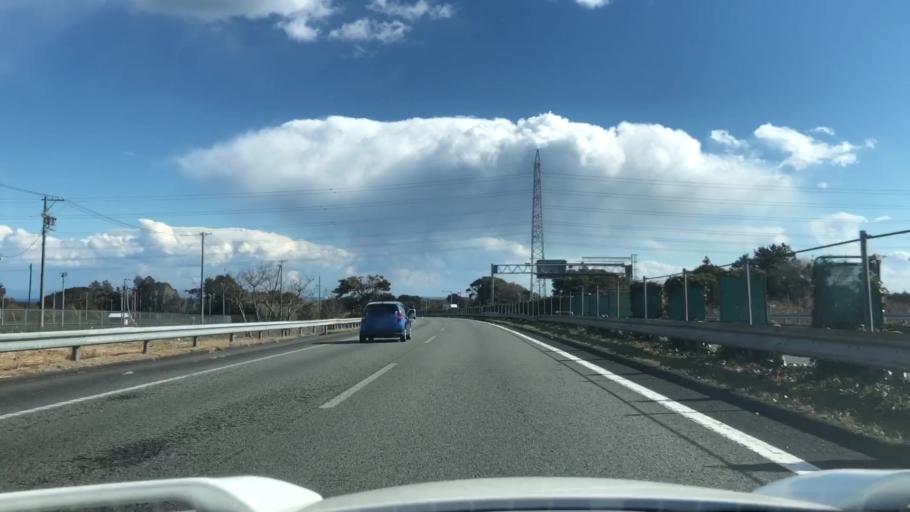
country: JP
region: Shizuoka
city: Shimada
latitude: 34.7571
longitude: 138.1702
